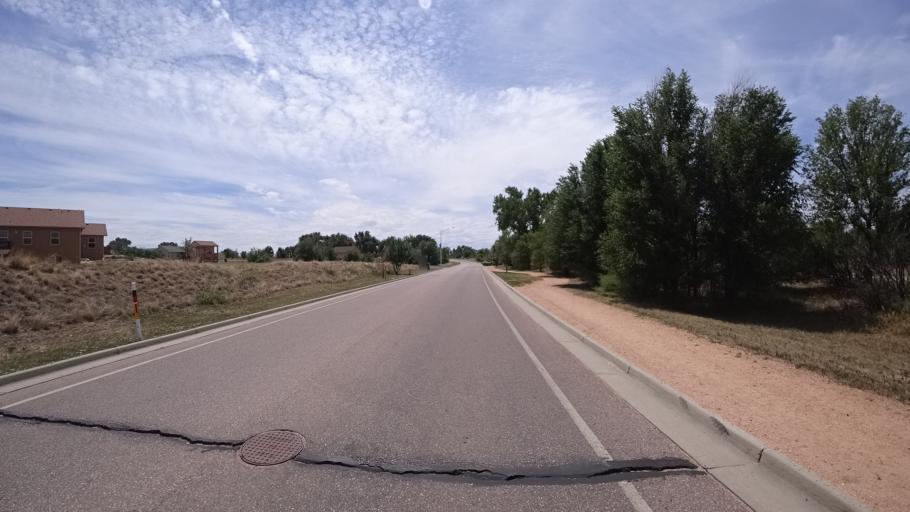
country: US
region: Colorado
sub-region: El Paso County
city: Fountain
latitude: 38.6870
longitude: -104.6862
